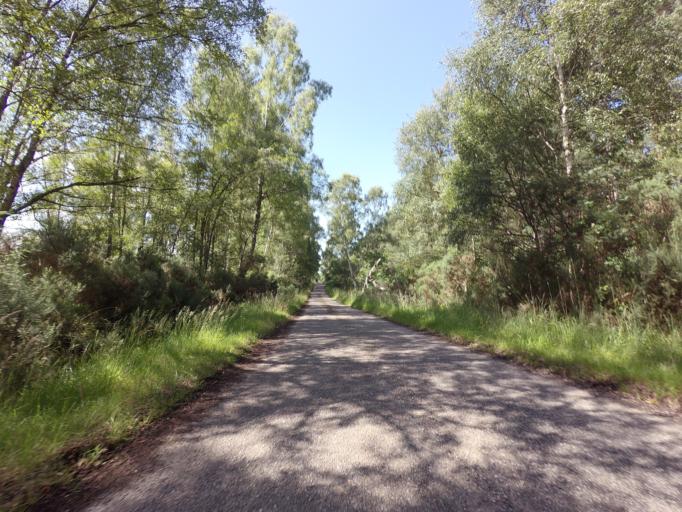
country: GB
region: Scotland
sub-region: Highland
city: Nairn
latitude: 57.5040
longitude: -3.9168
